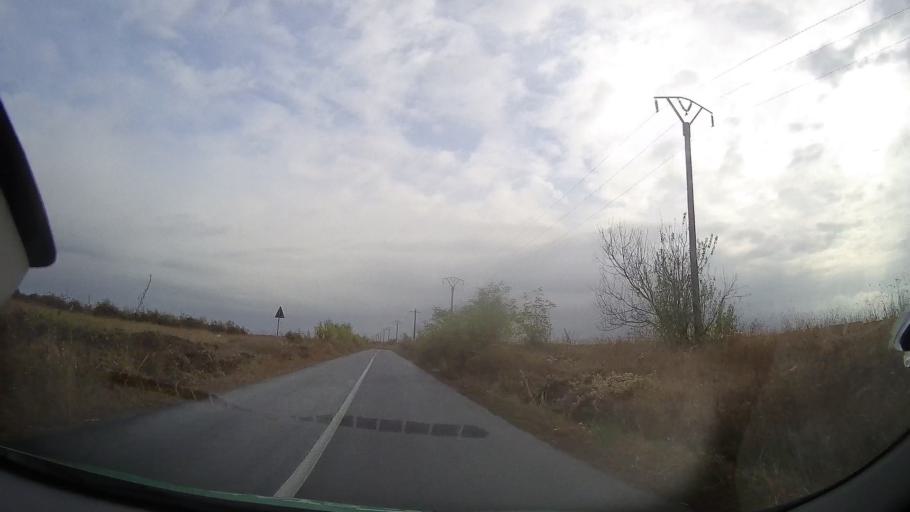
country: RO
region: Ialomita
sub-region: Comuna Maia
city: Maia
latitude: 44.7533
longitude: 26.3859
